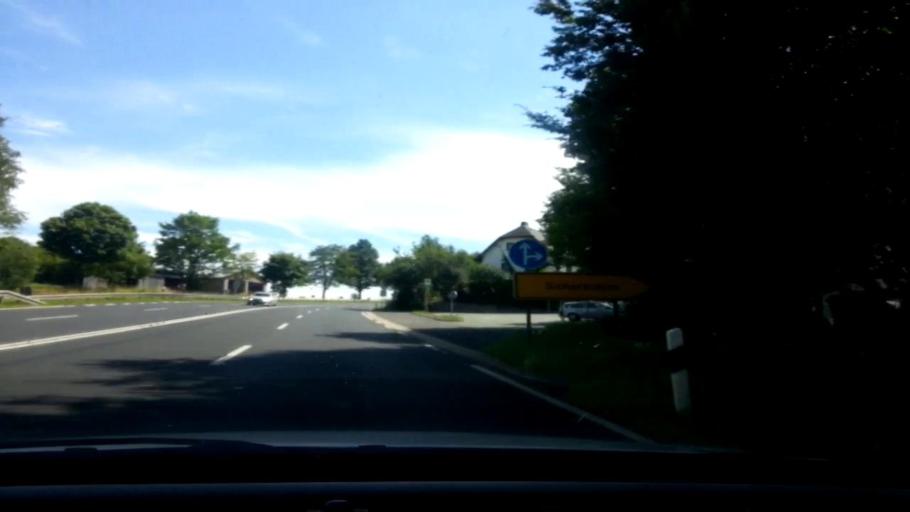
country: DE
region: Bavaria
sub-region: Upper Franconia
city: Bad Alexandersbad
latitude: 50.0183
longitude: 12.0378
